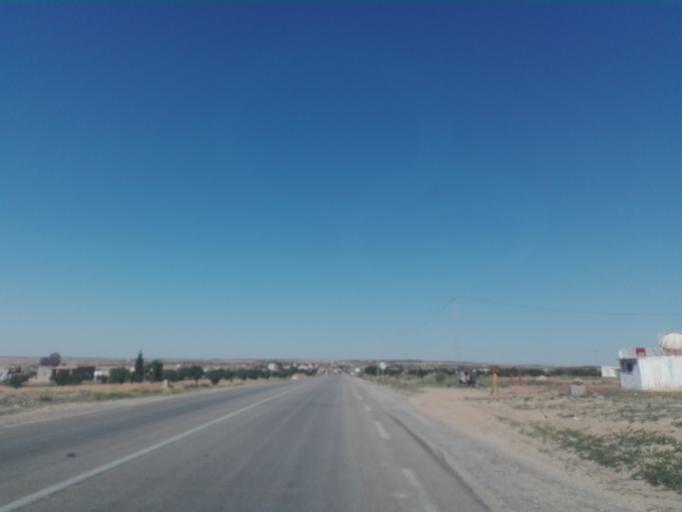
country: TN
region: Safaqis
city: Bi'r `Ali Bin Khalifah
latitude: 34.7405
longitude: 10.3912
